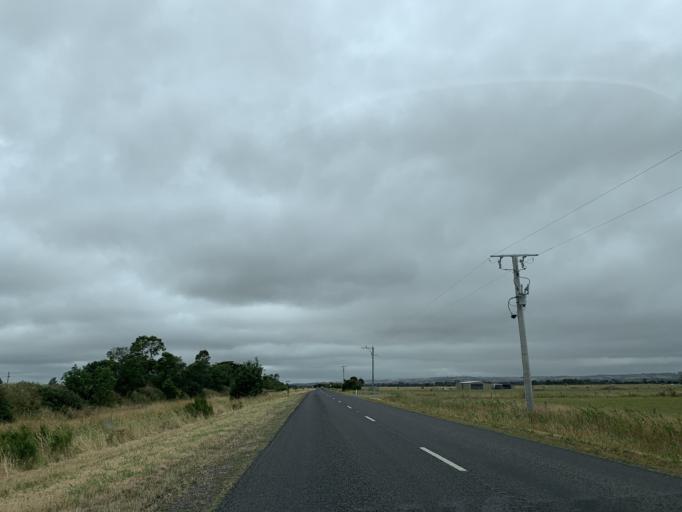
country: AU
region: Victoria
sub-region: Cardinia
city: Garfield
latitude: -38.1897
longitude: 145.6541
